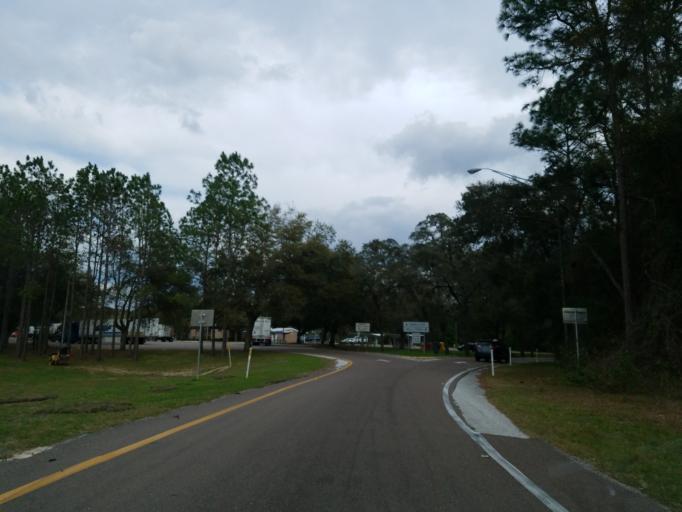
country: US
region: Florida
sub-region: Hernando County
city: Ridge Manor
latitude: 28.5834
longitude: -82.2139
